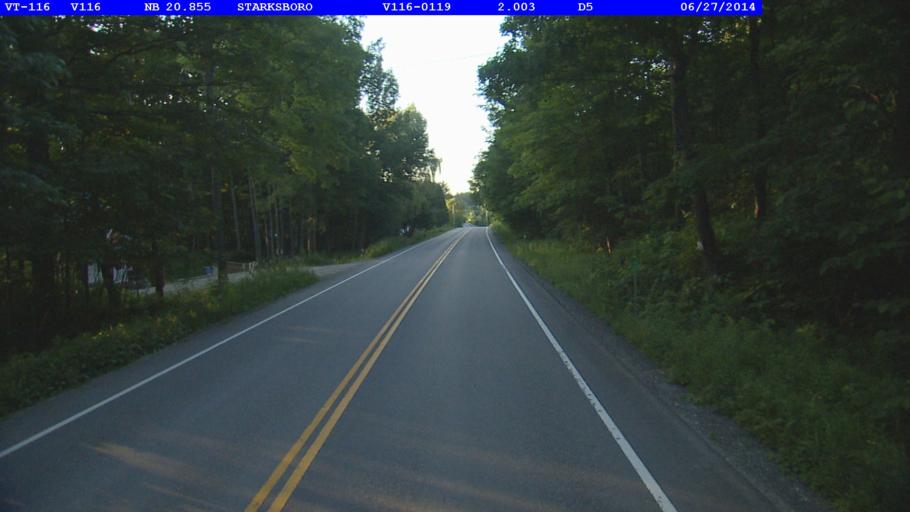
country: US
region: Vermont
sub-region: Addison County
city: Bristol
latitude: 44.2135
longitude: -73.0551
